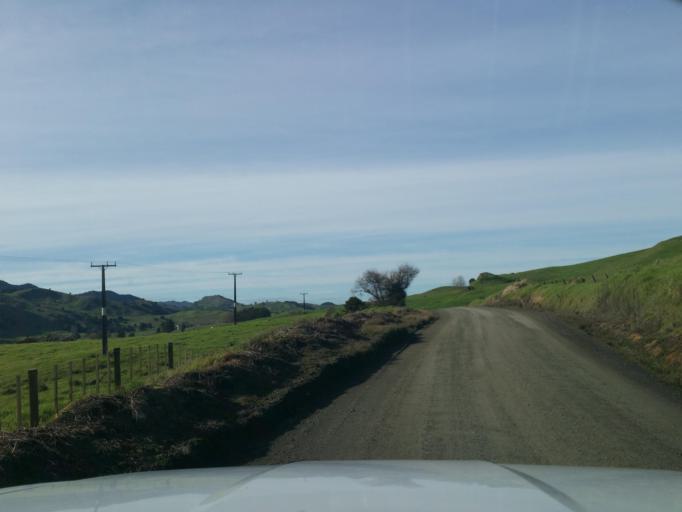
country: NZ
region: Northland
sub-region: Kaipara District
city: Dargaville
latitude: -35.8231
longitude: 173.9154
